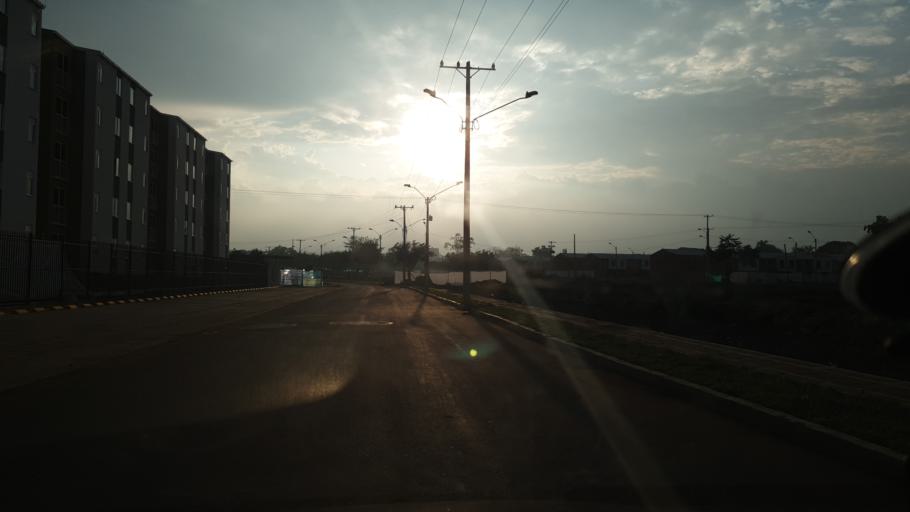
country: CO
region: Valle del Cauca
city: Jamundi
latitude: 3.3454
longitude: -76.5169
